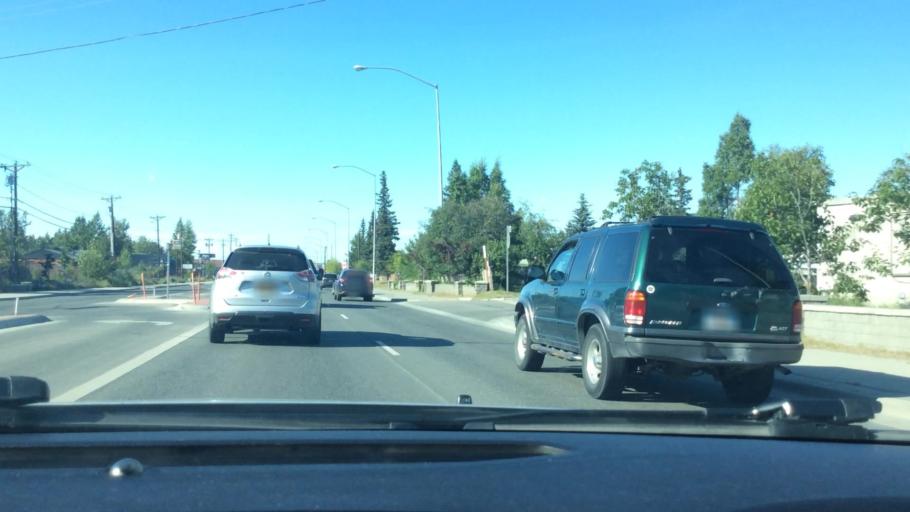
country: US
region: Alaska
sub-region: Anchorage Municipality
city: Elmendorf Air Force Base
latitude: 61.2139
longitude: -149.7334
